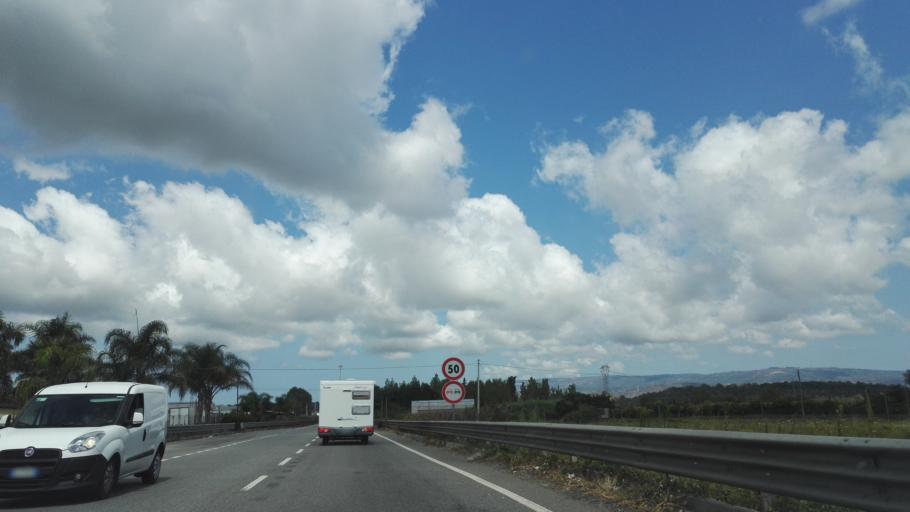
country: IT
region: Calabria
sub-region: Provincia di Reggio Calabria
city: Rosarno
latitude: 38.4642
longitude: 16.0131
